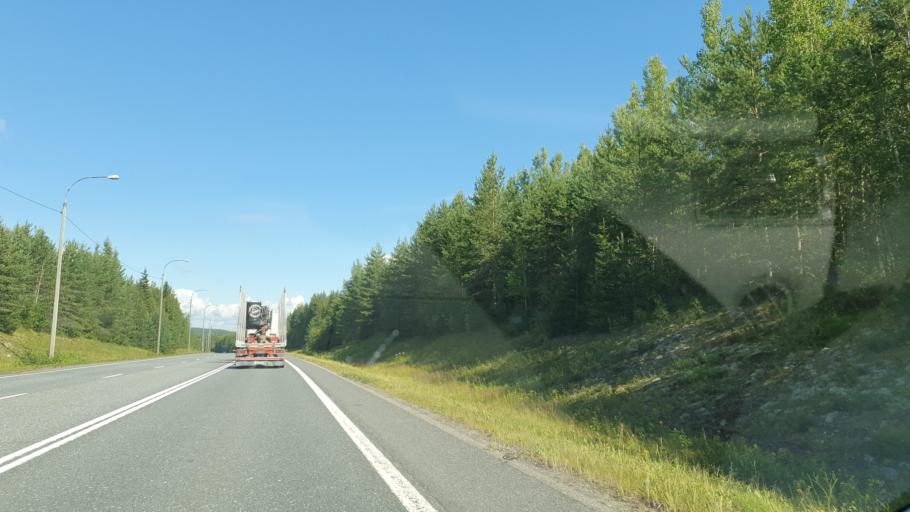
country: FI
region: Northern Savo
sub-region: Ylae-Savo
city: Iisalmi
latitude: 63.6176
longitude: 27.2226
